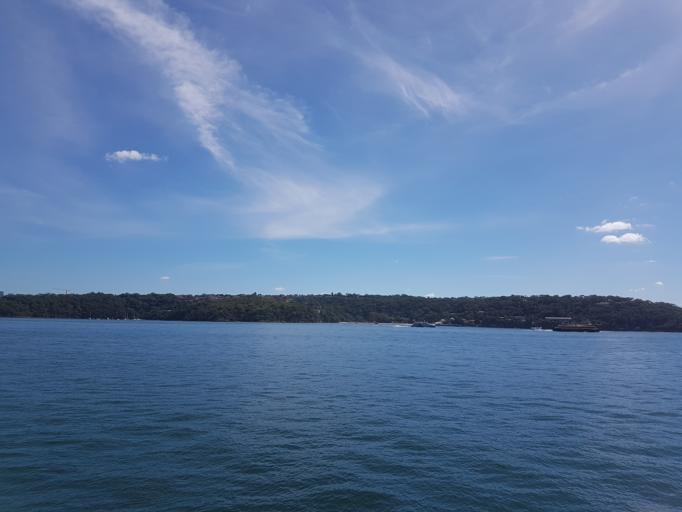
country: AU
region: New South Wales
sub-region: Woollahra
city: Point Piper
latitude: -33.8495
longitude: 151.2633
